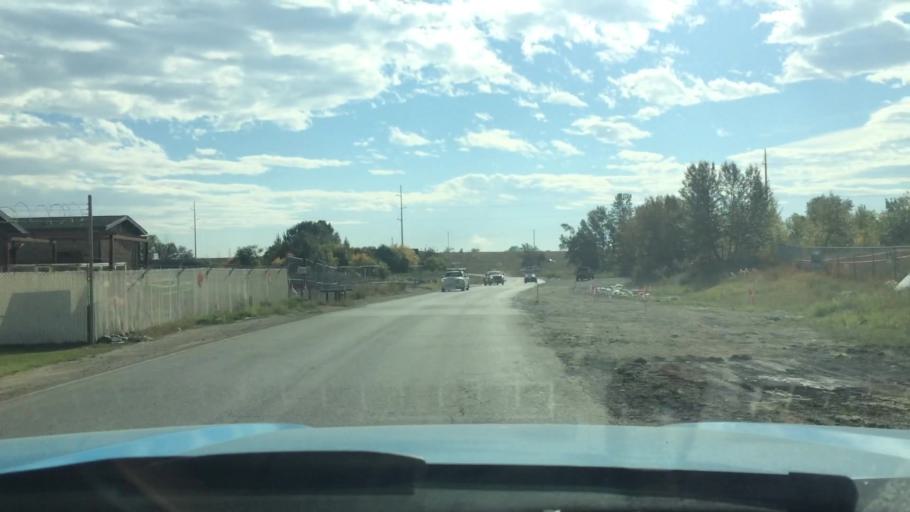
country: CA
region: Alberta
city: Calgary
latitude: 51.0087
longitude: -114.0308
